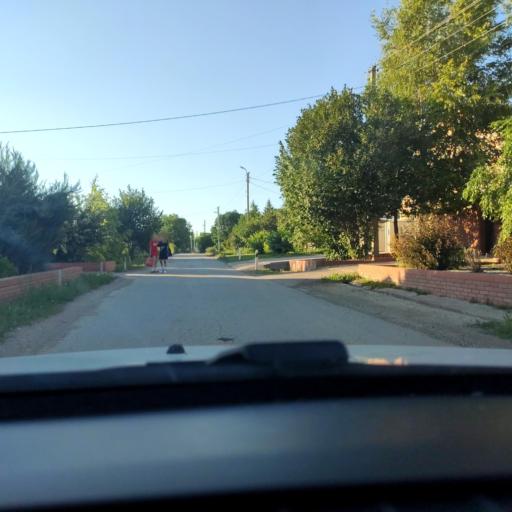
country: RU
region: Samara
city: Kinel'
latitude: 53.2702
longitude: 50.5926
